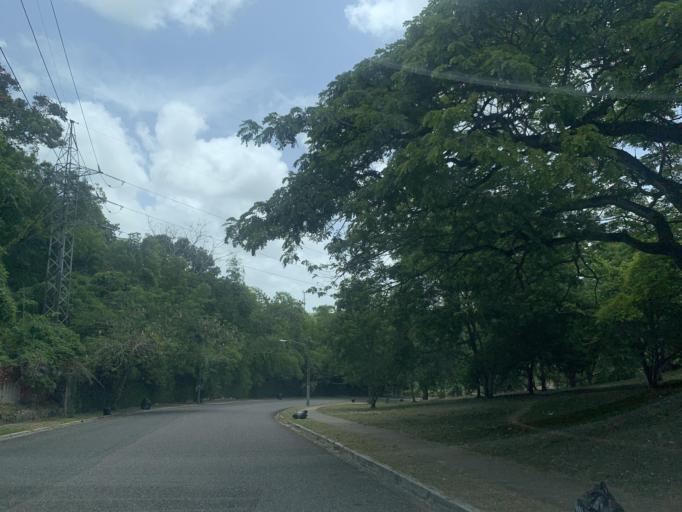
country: DO
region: Nacional
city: La Agustina
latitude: 18.5010
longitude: -69.9480
